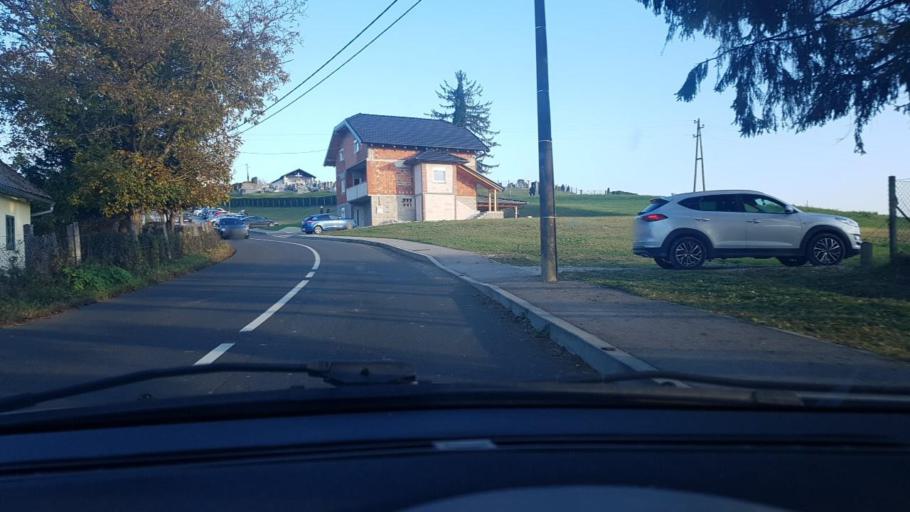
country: SI
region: Rogatec
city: Rogatec
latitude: 46.2140
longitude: 15.6691
